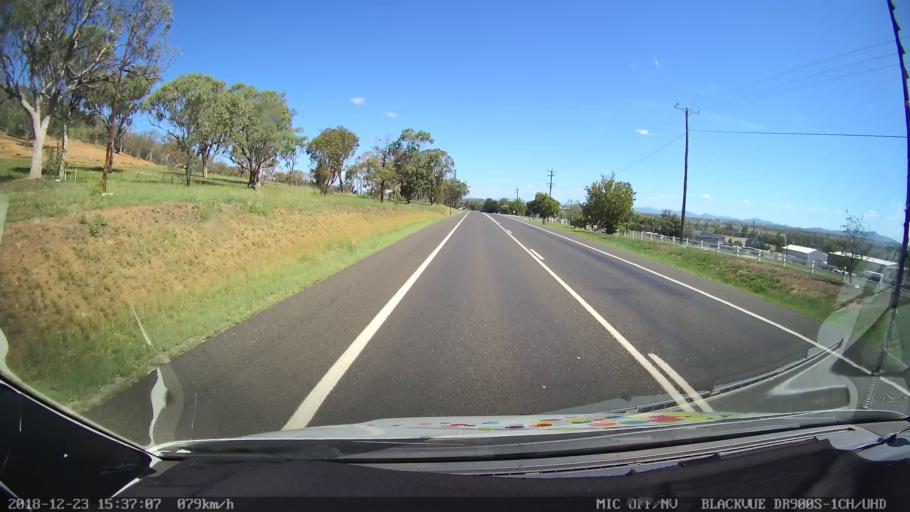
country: AU
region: New South Wales
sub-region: Tamworth Municipality
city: Tamworth
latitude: -31.0487
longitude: 150.8890
